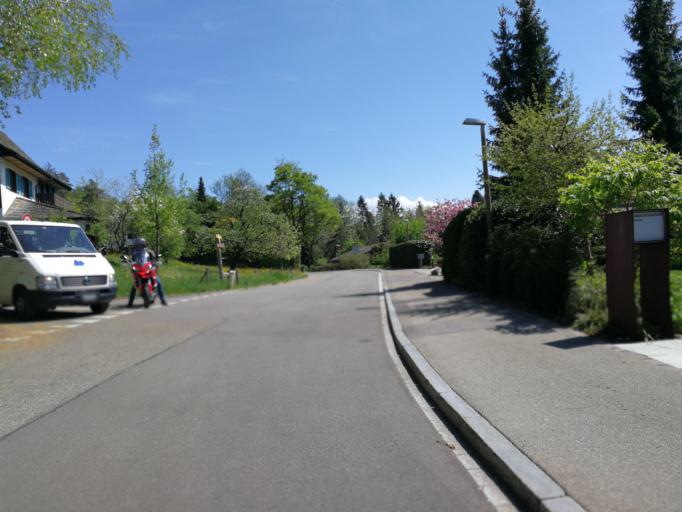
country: CH
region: Zurich
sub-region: Bezirk Meilen
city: Maennedorf / Dorfkern
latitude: 47.2687
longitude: 8.6911
